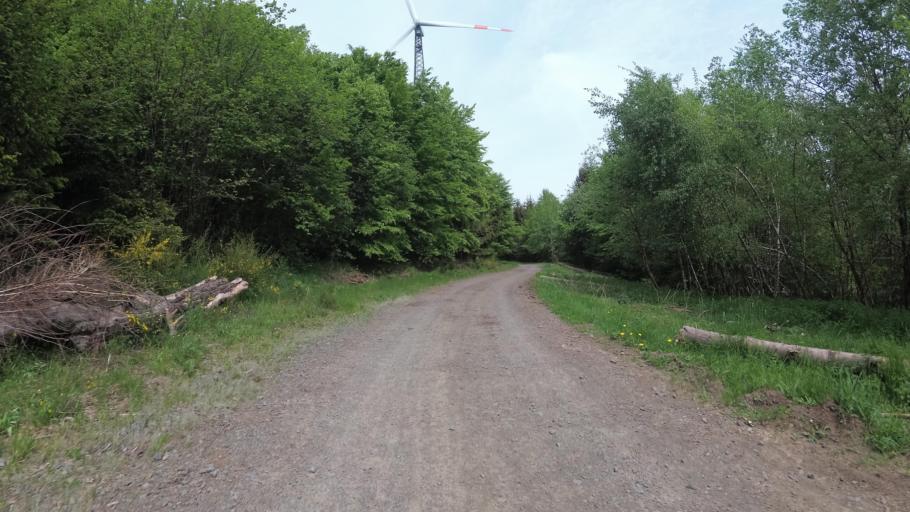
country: DE
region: Rheinland-Pfalz
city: Eckersweiler
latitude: 49.5508
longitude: 7.2753
